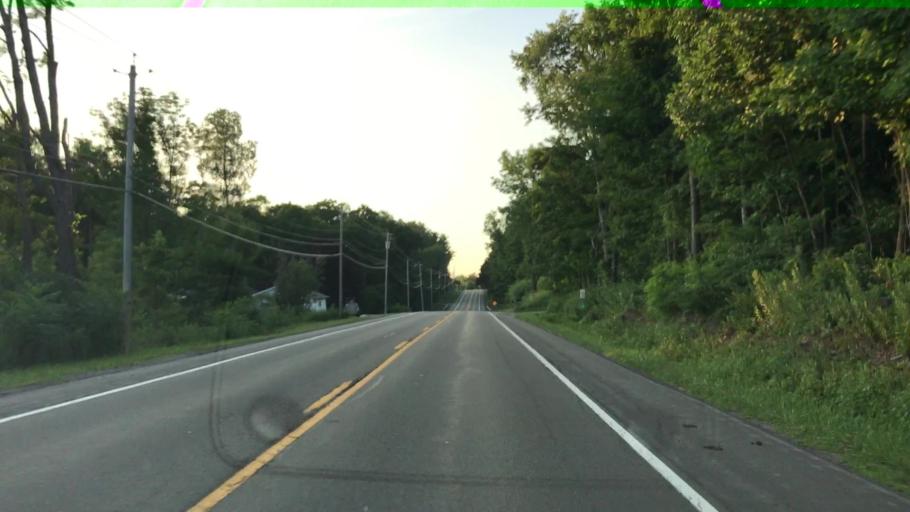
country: US
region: New York
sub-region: Chautauqua County
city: Mayville
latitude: 42.2542
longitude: -79.4662
